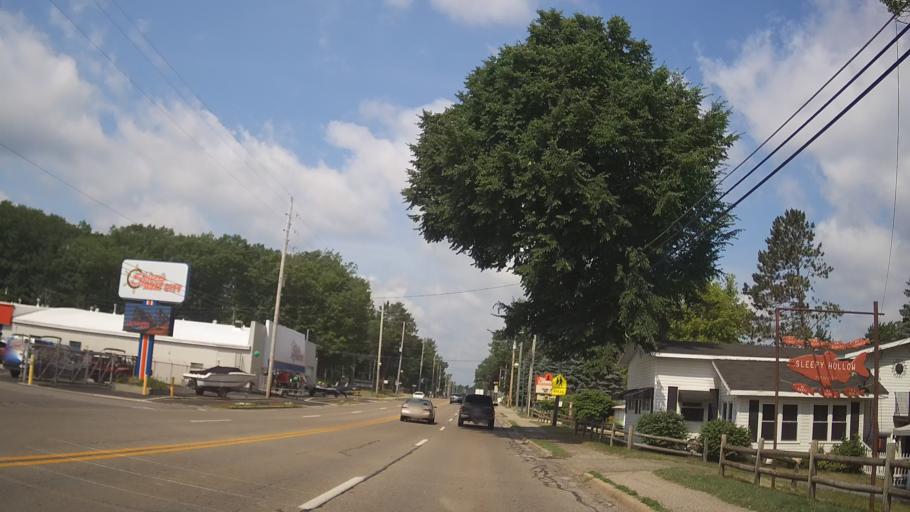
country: US
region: Michigan
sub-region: Roscommon County
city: Houghton Lake
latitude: 44.2985
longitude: -84.7211
